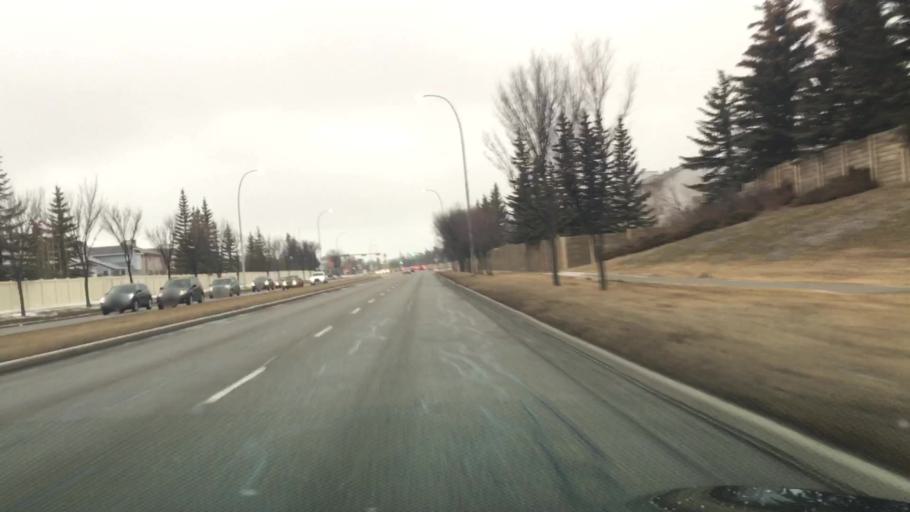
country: CA
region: Alberta
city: Calgary
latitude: 51.1389
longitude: -114.1532
